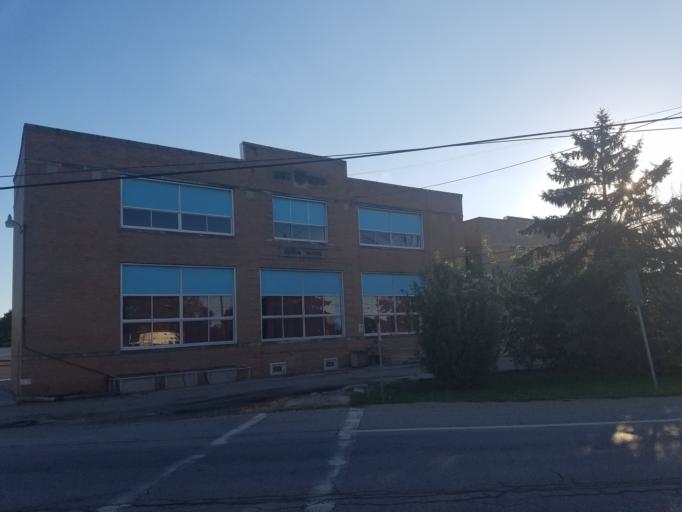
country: US
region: Ohio
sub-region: Morrow County
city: Mount Gilead
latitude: 40.5541
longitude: -82.8621
